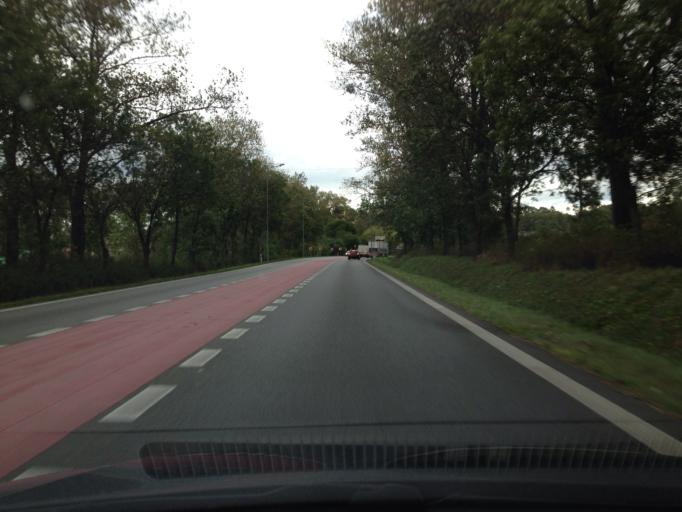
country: PL
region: Kujawsko-Pomorskie
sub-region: Powiat lipnowski
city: Lipno
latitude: 52.8581
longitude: 19.2447
